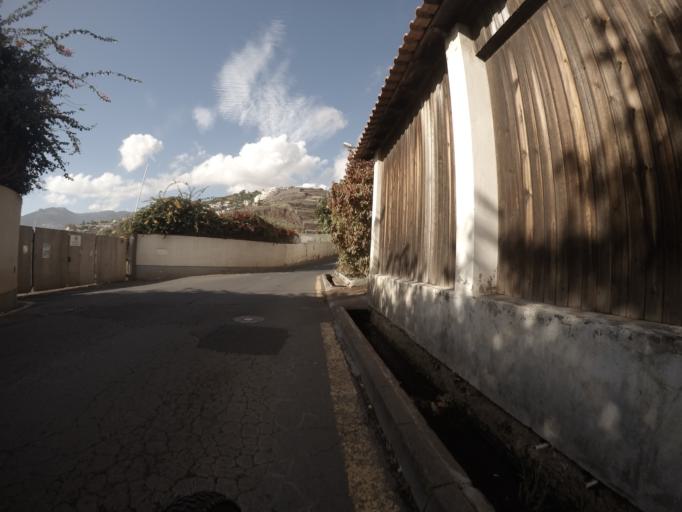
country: PT
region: Madeira
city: Camara de Lobos
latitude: 32.6401
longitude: -16.9506
